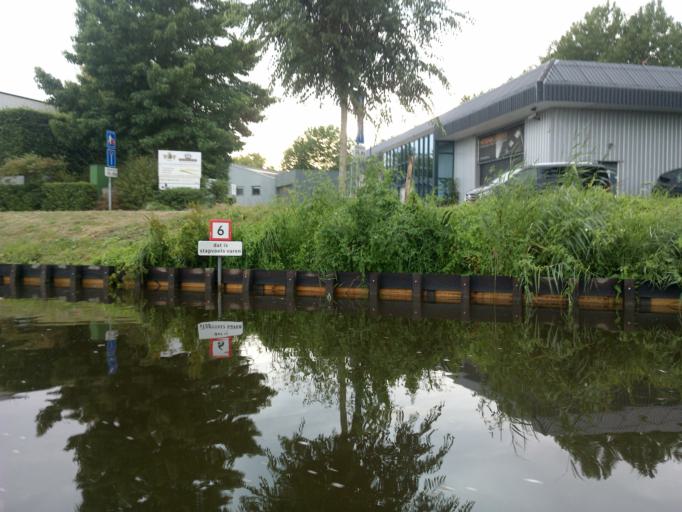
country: NL
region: North Holland
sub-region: Gemeente Wijdemeren
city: Nieuw-Loosdrecht
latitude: 52.2096
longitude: 5.1145
